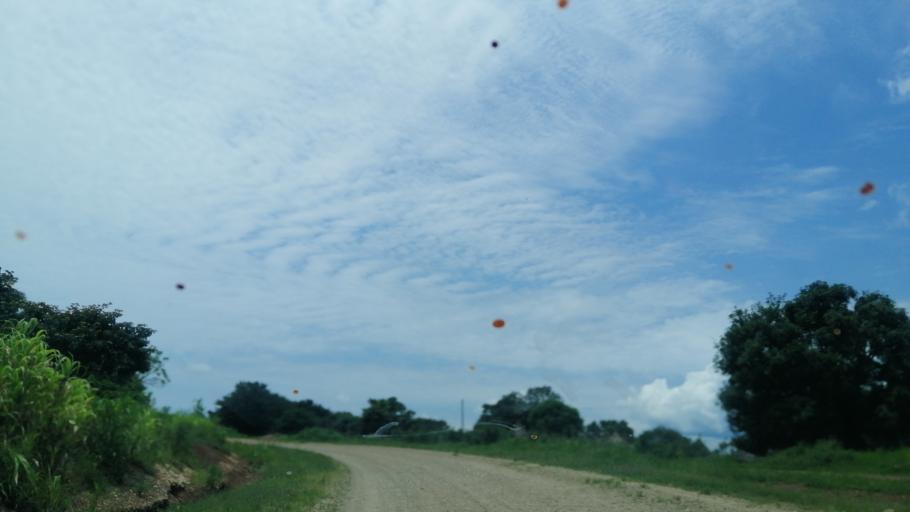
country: ET
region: Oromiya
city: Mendi
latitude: 10.1673
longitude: 35.0934
